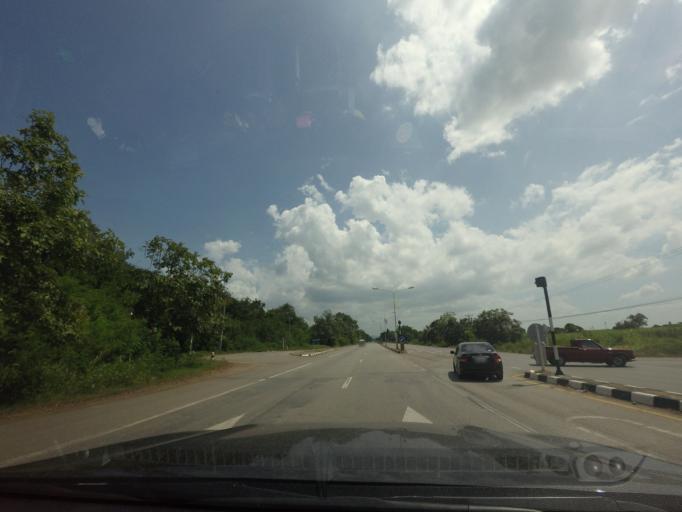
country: TH
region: Phetchabun
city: Phetchabun
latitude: 16.2461
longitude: 101.0725
